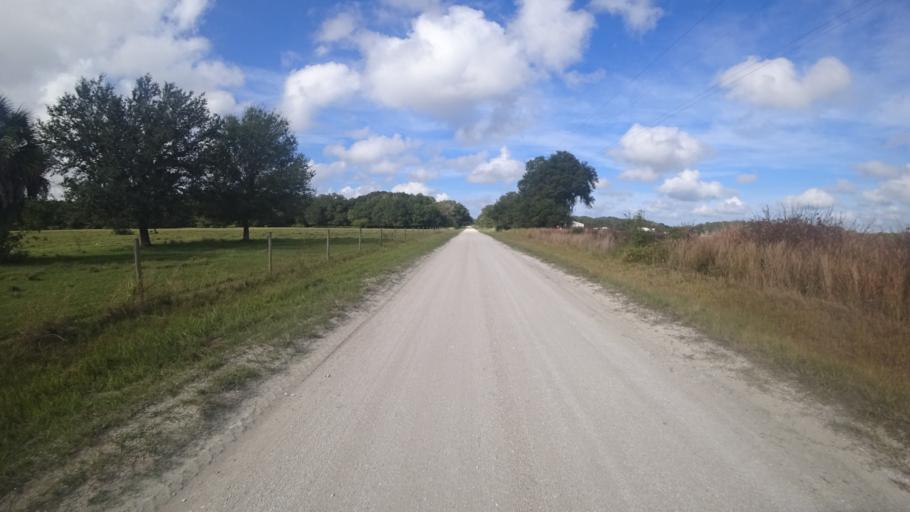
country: US
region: Florida
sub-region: Hillsborough County
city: Ruskin
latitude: 27.6127
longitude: -82.4047
